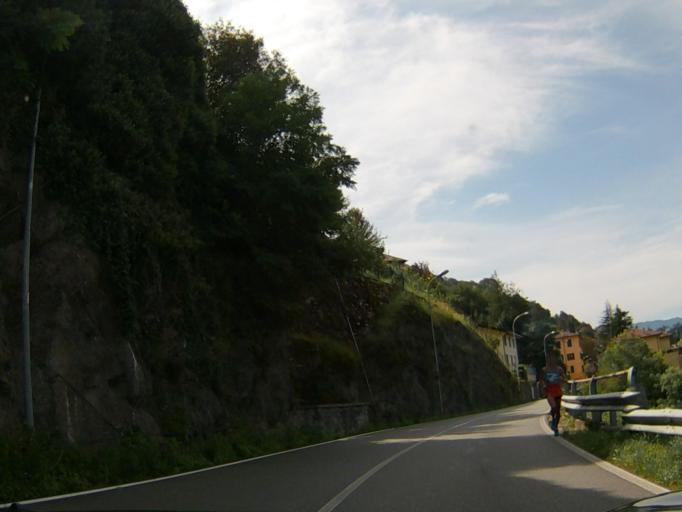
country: IT
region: Lombardy
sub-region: Provincia di Lecco
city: Bellano
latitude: 46.0537
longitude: 9.3125
